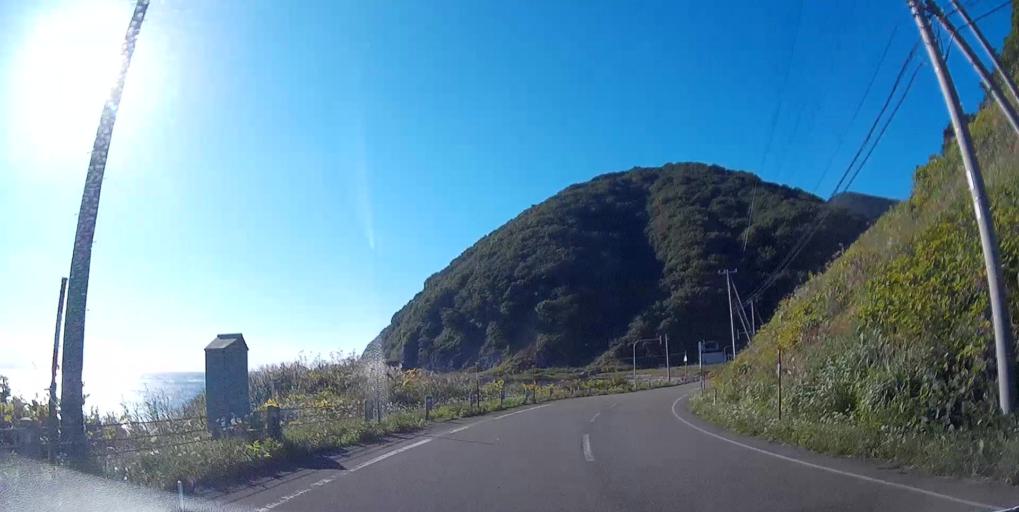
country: JP
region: Hokkaido
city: Kamiiso
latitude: 42.2496
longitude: 139.7846
